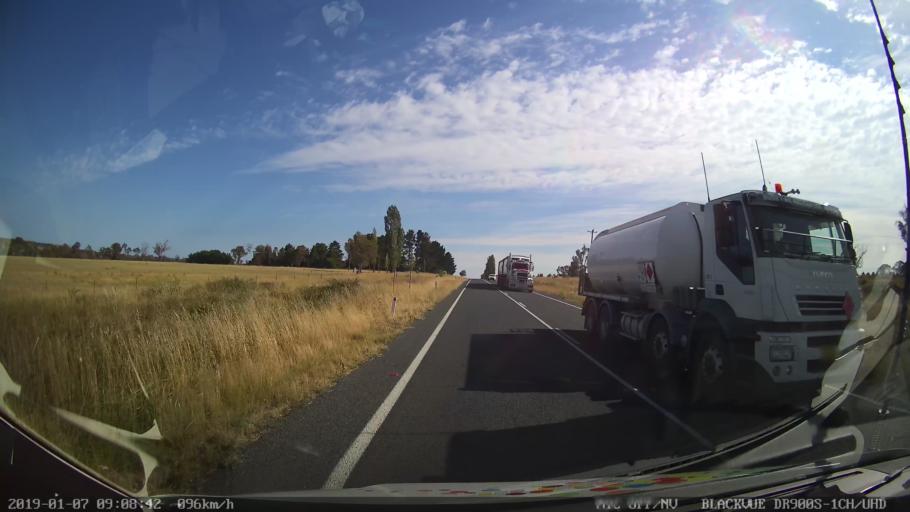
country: AU
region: New South Wales
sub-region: Armidale Dumaresq
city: Armidale
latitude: -30.6684
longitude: 151.4842
